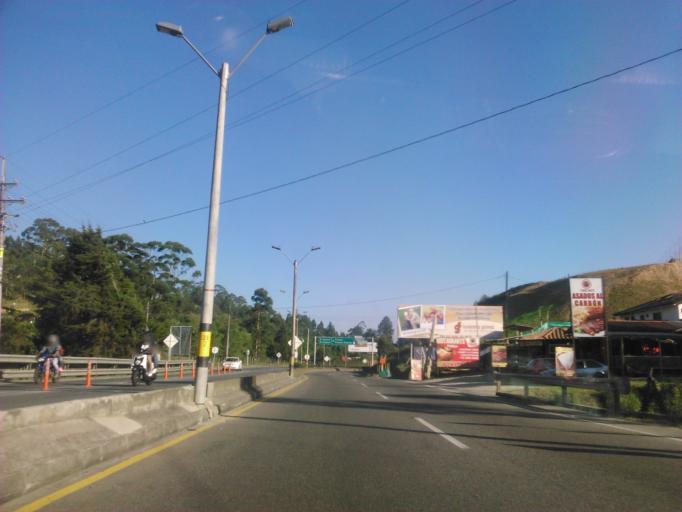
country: CO
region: Antioquia
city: Guarne
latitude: 6.2915
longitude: -75.4499
